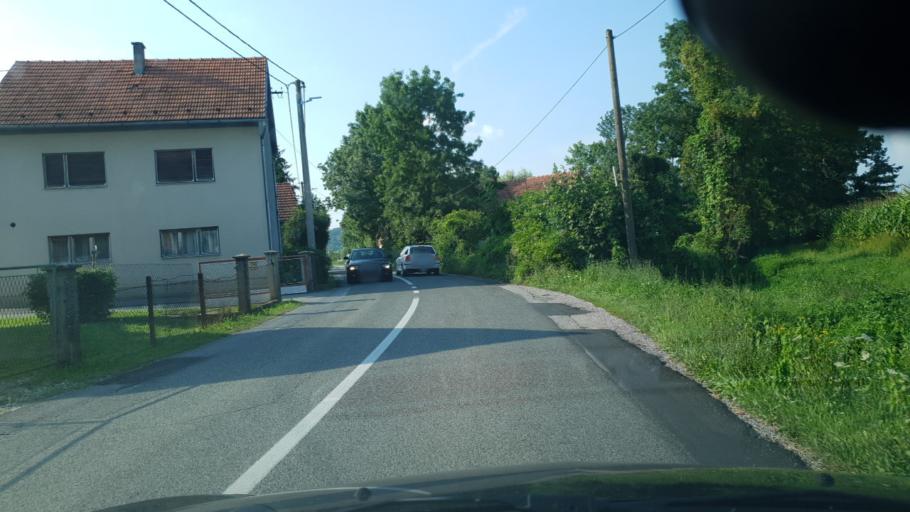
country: HR
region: Krapinsko-Zagorska
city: Oroslavje
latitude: 45.9996
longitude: 15.8846
